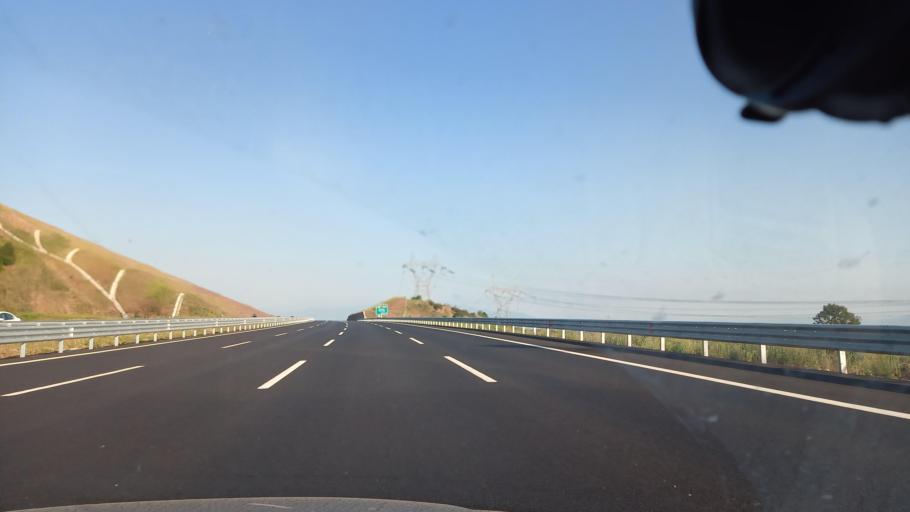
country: TR
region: Sakarya
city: Adapazari
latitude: 40.8229
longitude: 30.4005
